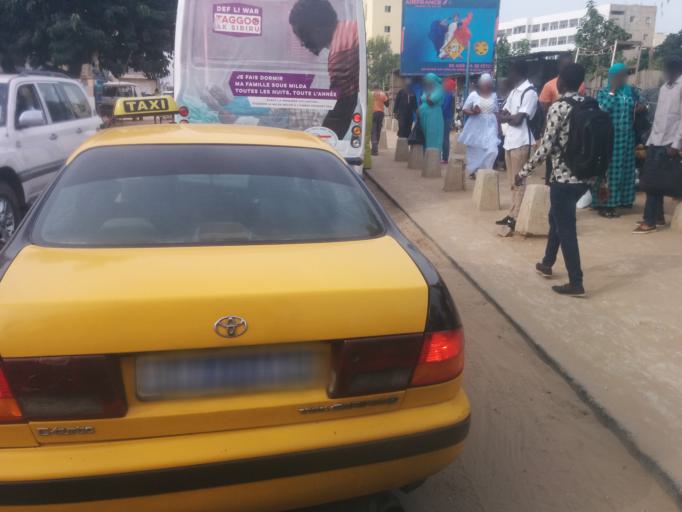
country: SN
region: Dakar
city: Grand Dakar
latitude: 14.7413
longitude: -17.4517
